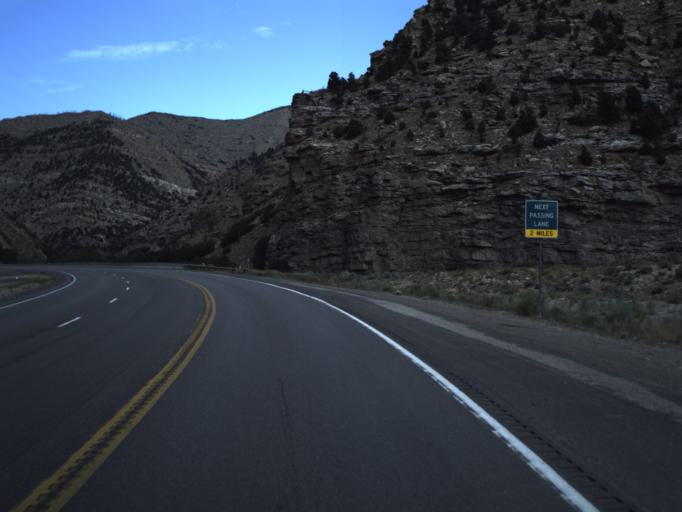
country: US
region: Utah
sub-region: Carbon County
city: Helper
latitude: 39.7503
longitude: -110.8850
